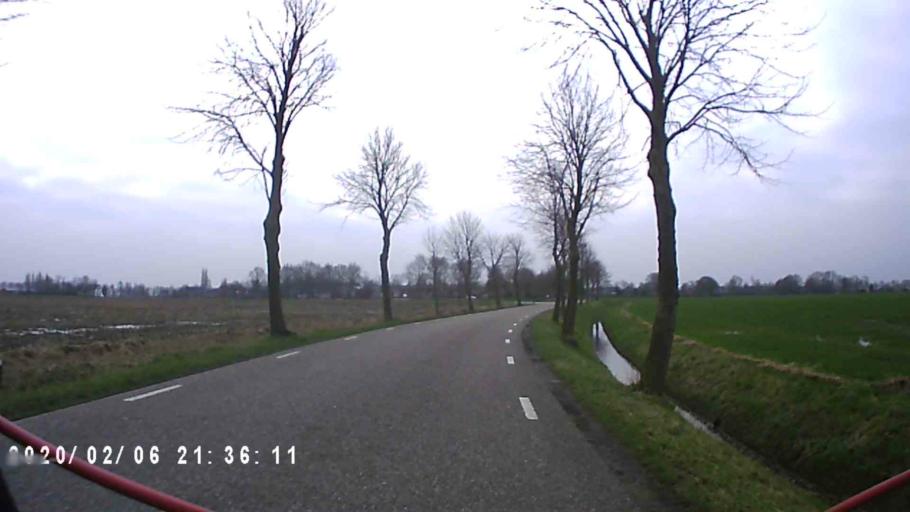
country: NL
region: Groningen
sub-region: Gemeente Zuidhorn
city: Noordhorn
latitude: 53.2683
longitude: 6.3940
